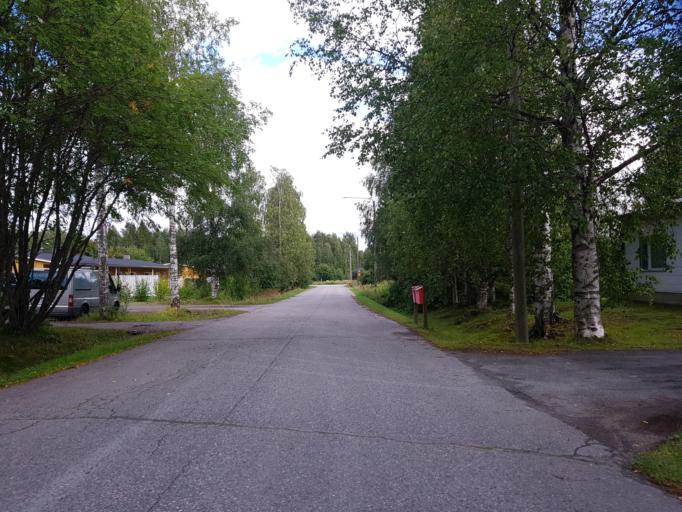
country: FI
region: Kainuu
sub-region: Kehys-Kainuu
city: Kuhmo
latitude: 64.1251
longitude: 29.5430
